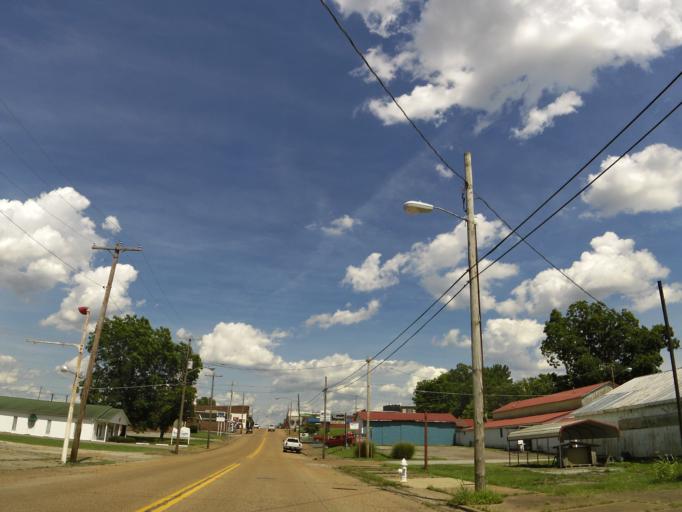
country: US
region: Tennessee
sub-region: Gibson County
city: Trenton
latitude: 35.9808
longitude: -88.9454
